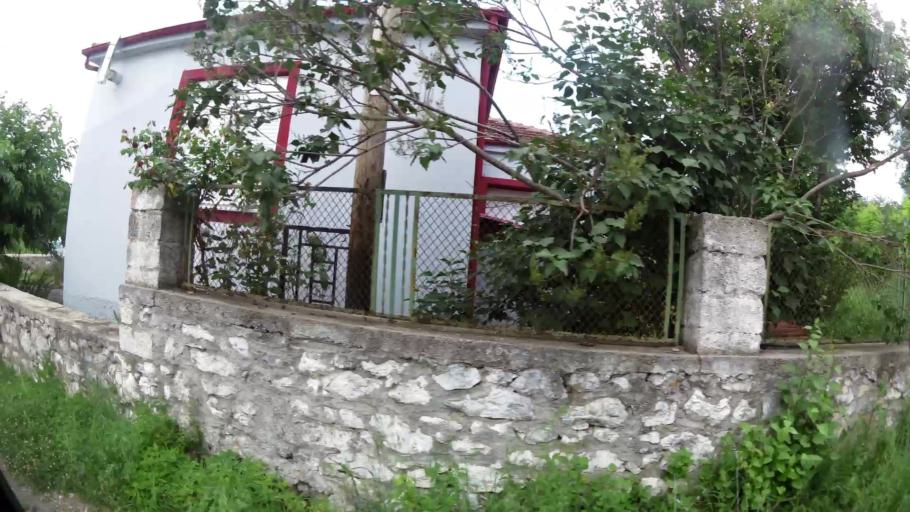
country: GR
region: West Macedonia
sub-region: Nomos Kozanis
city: Koila
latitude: 40.3474
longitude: 21.8304
